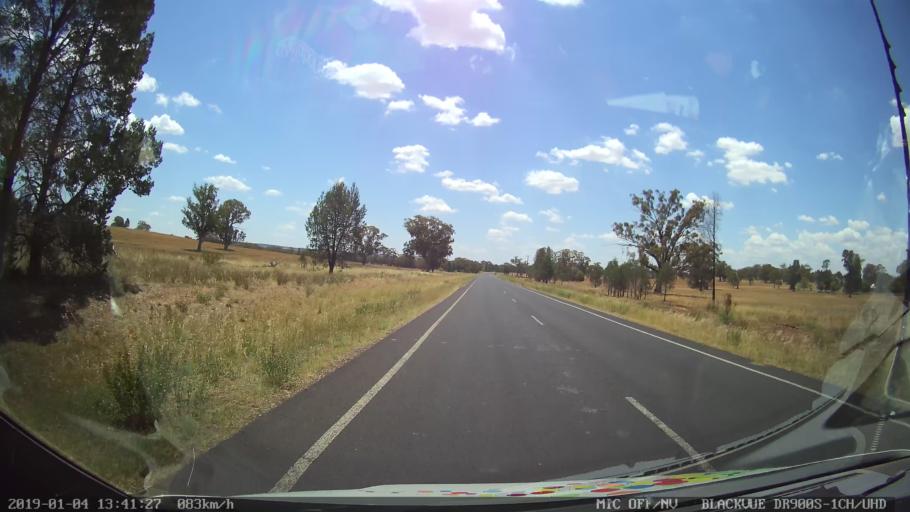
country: AU
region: New South Wales
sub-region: Dubbo Municipality
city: Dubbo
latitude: -32.5021
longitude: 148.5535
